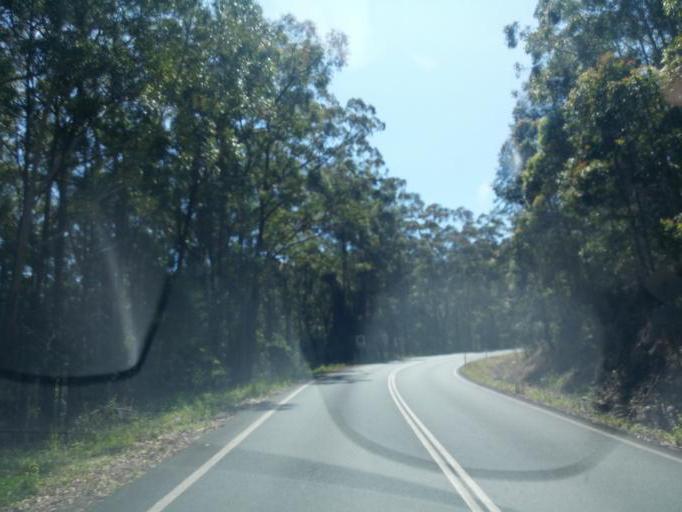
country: AU
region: New South Wales
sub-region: Great Lakes
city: Bulahdelah
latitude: -32.4008
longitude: 152.3007
